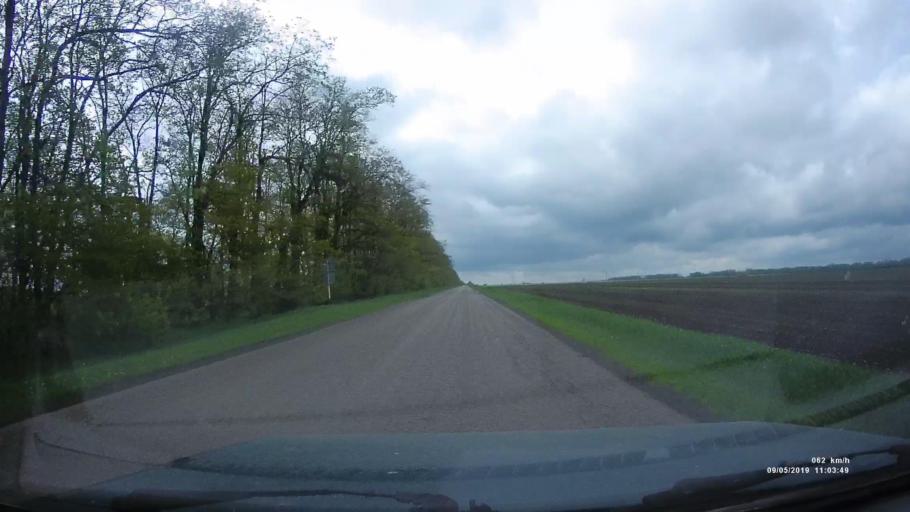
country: RU
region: Krasnodarskiy
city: Kanelovskaya
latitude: 46.8242
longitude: 39.2101
